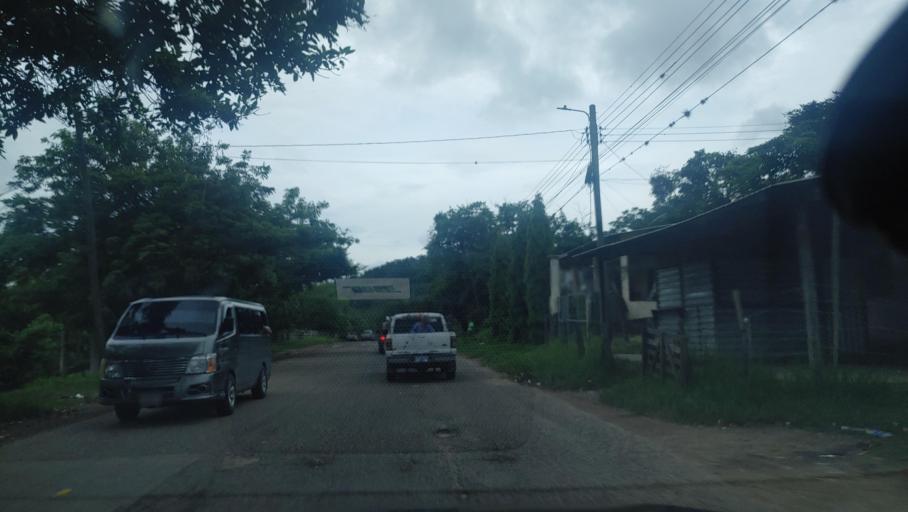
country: HN
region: Choluteca
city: San Marcos de Colon
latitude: 13.3793
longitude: -86.8733
